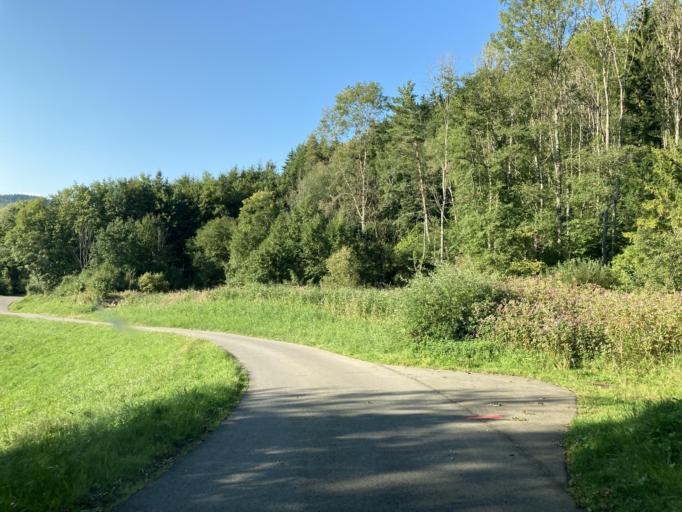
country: DE
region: Baden-Wuerttemberg
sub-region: Freiburg Region
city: Blumberg
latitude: 47.8296
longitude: 8.5079
